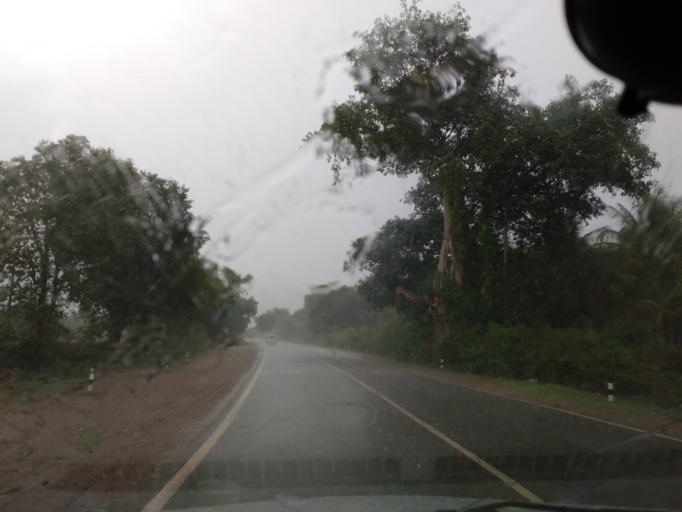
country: IN
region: Karnataka
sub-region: Tumkur
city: Chiknayakanhalli
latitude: 13.3056
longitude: 76.6072
